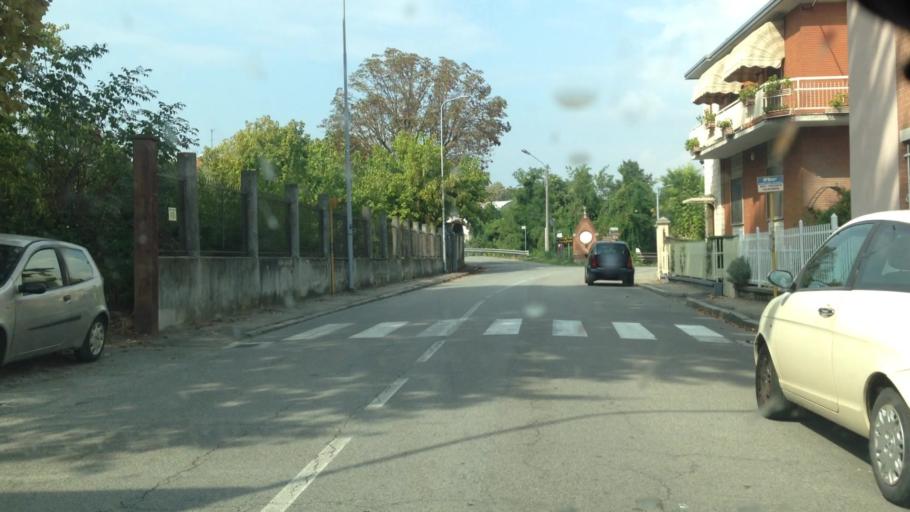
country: IT
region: Piedmont
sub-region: Provincia di Asti
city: Asti
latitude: 44.9085
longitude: 8.2122
